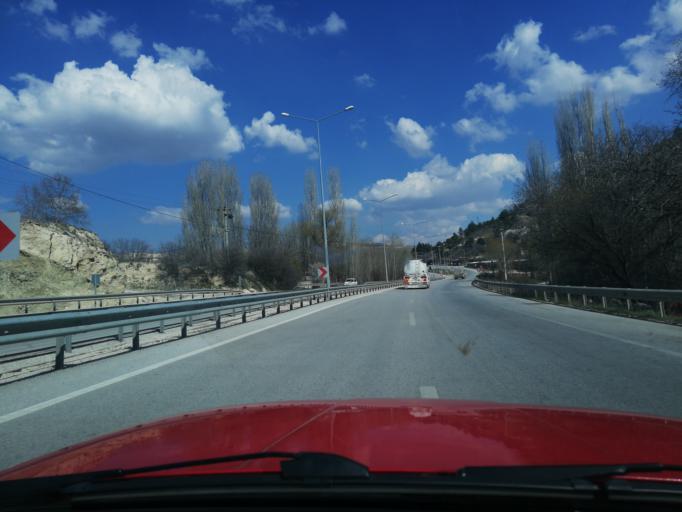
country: TR
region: Burdur
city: Burdur
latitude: 37.6983
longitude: 30.3335
